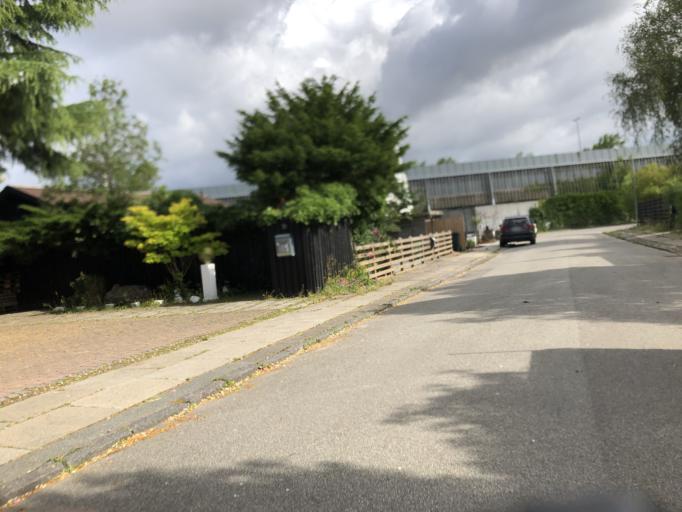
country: DK
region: Capital Region
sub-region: Gladsaxe Municipality
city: Buddinge
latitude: 55.7510
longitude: 12.4844
